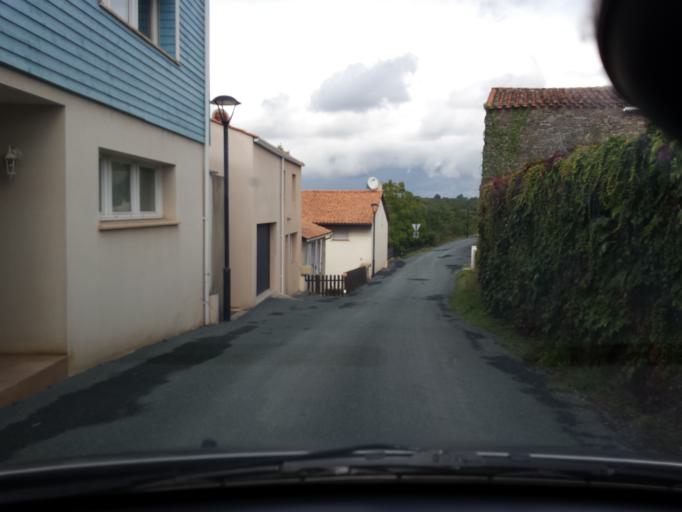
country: FR
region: Pays de la Loire
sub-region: Departement de la Vendee
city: Saint-Vincent-sur-Graon
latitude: 46.5167
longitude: -1.3876
